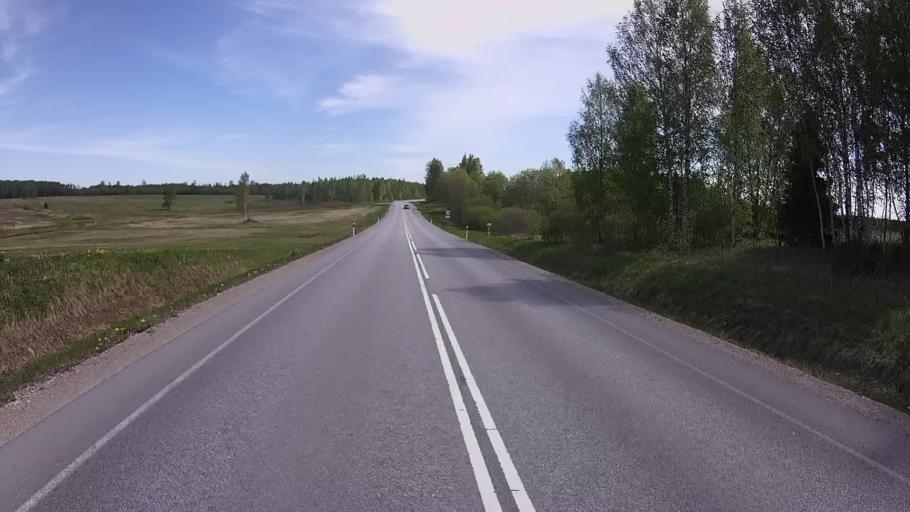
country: EE
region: Valgamaa
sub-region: Valga linn
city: Valga
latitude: 57.7222
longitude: 26.1925
